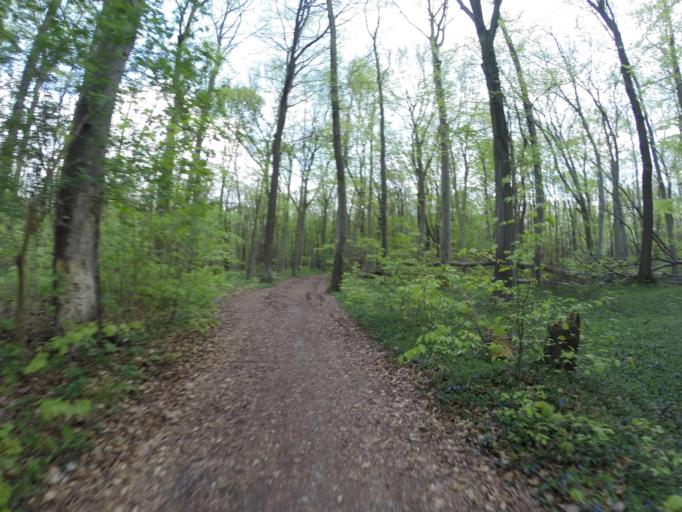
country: DE
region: Thuringia
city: Golmsdorf
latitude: 50.9589
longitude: 11.6517
